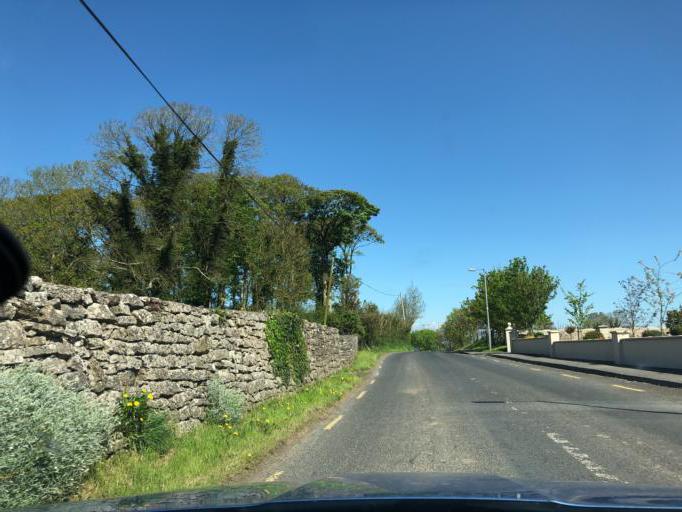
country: IE
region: Connaught
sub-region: County Galway
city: Portumna
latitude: 53.1403
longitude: -8.3670
